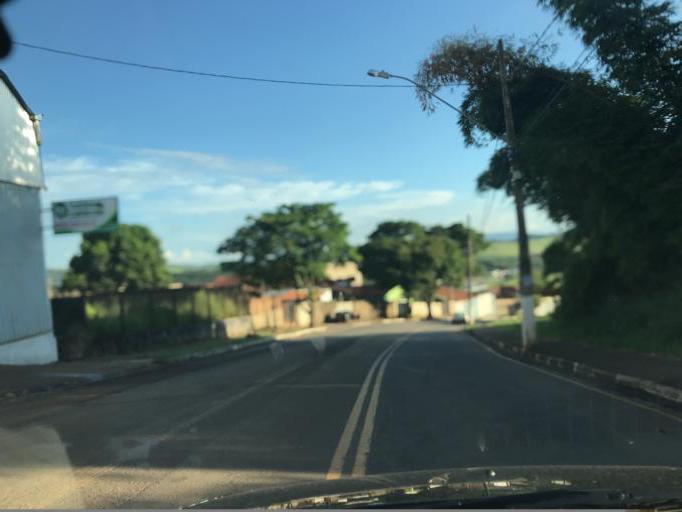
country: BR
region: Minas Gerais
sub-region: Tres Coracoes
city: Tres Coracoes
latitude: -21.6943
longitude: -45.2448
